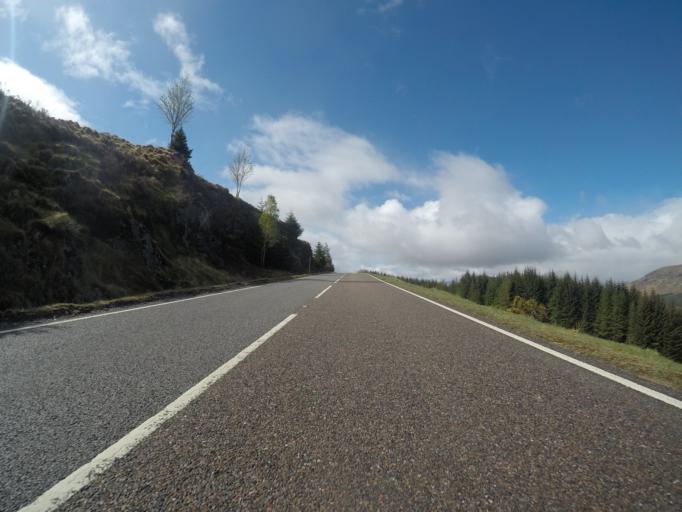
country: GB
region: Scotland
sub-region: Highland
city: Spean Bridge
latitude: 57.1016
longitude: -4.9910
